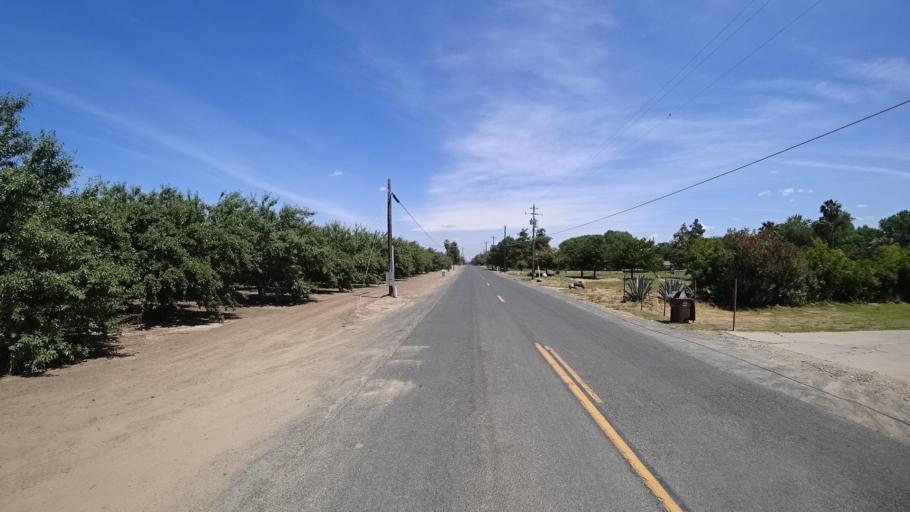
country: US
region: California
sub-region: Kings County
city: Lemoore
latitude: 36.2837
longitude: -119.7762
